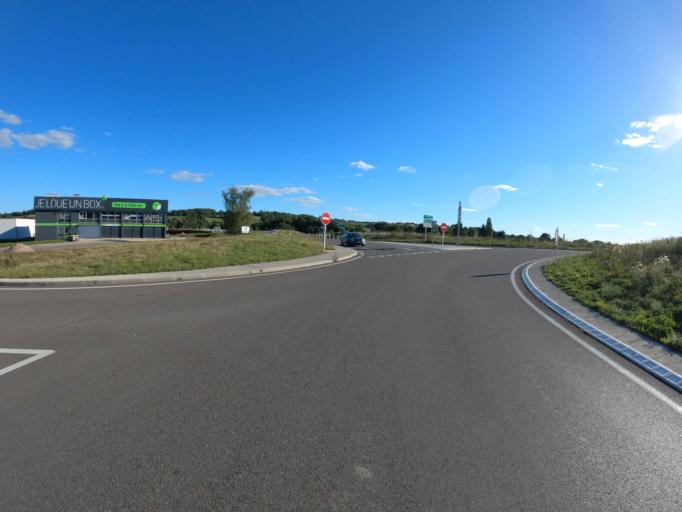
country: FR
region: Bourgogne
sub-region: Departement de Saone-et-Loire
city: Blanzy
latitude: 46.7038
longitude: 4.4111
